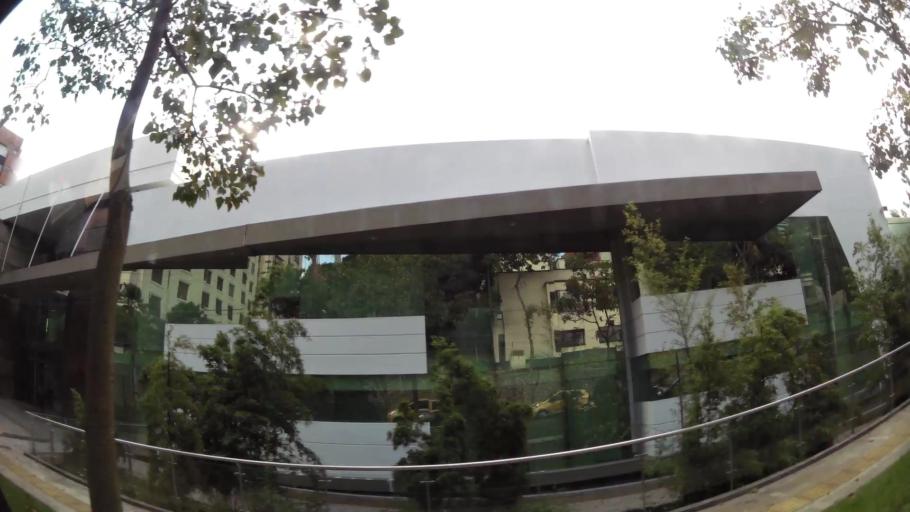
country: CO
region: Antioquia
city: Itagui
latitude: 6.2065
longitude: -75.5729
